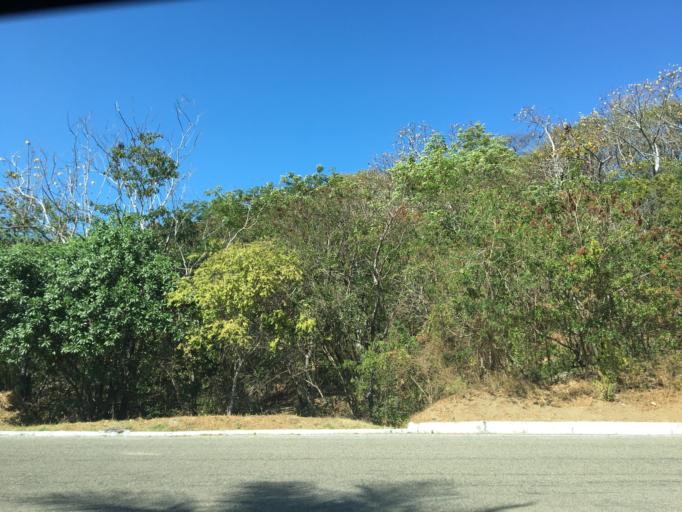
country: MX
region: Oaxaca
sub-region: Santa Maria Huatulco
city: Crucecita
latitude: 15.7858
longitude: -96.0601
